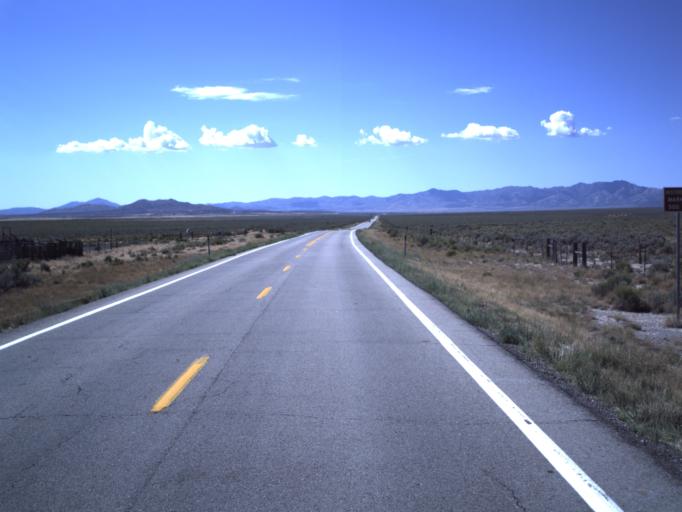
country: US
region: Utah
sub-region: Tooele County
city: Tooele
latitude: 40.2540
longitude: -112.3988
